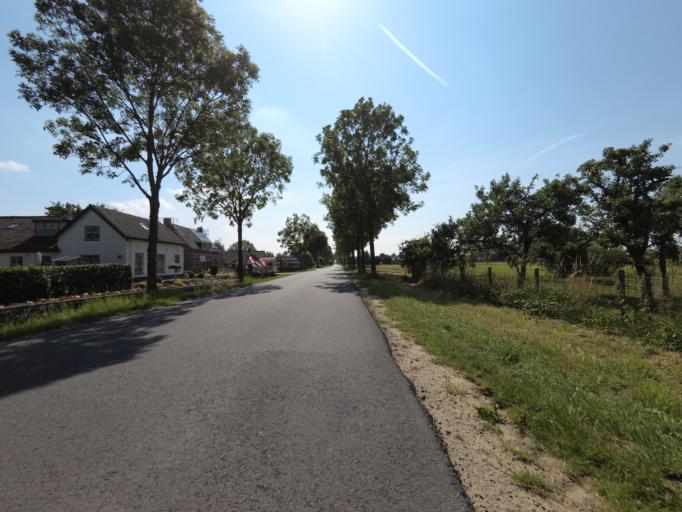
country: NL
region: South Holland
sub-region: Gemeente Leerdam
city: Leerdam
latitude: 51.9329
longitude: 5.1184
